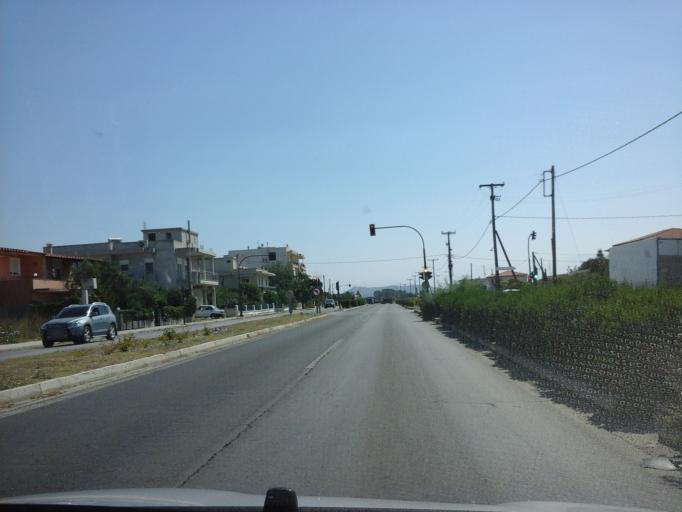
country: GR
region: East Macedonia and Thrace
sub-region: Nomos Evrou
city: Alexandroupoli
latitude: 40.8561
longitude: 25.9352
